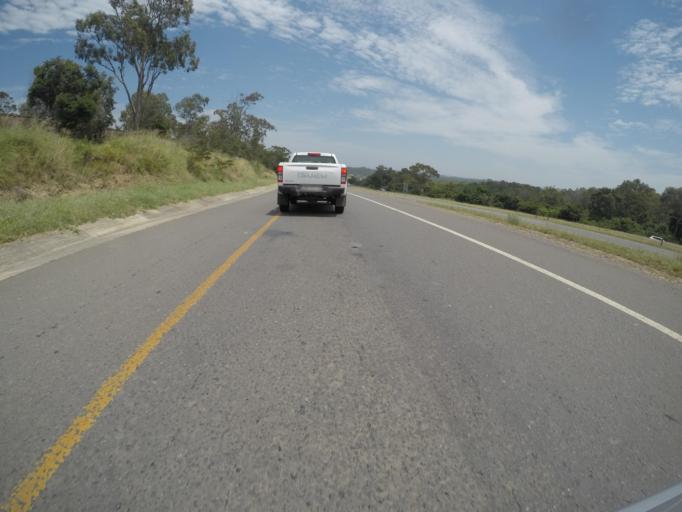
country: ZA
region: Eastern Cape
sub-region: Buffalo City Metropolitan Municipality
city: East London
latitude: -32.9397
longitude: 27.9499
